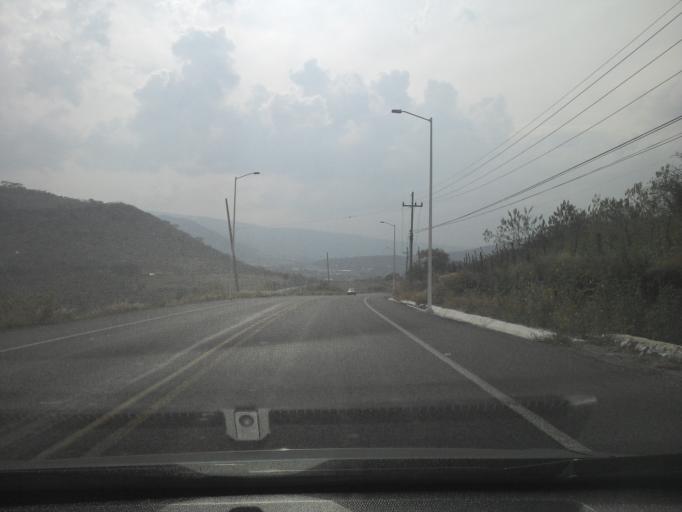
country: MX
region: Jalisco
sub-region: Tlajomulco de Zuniga
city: Lomas del Sur
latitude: 20.4843
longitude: -103.4286
